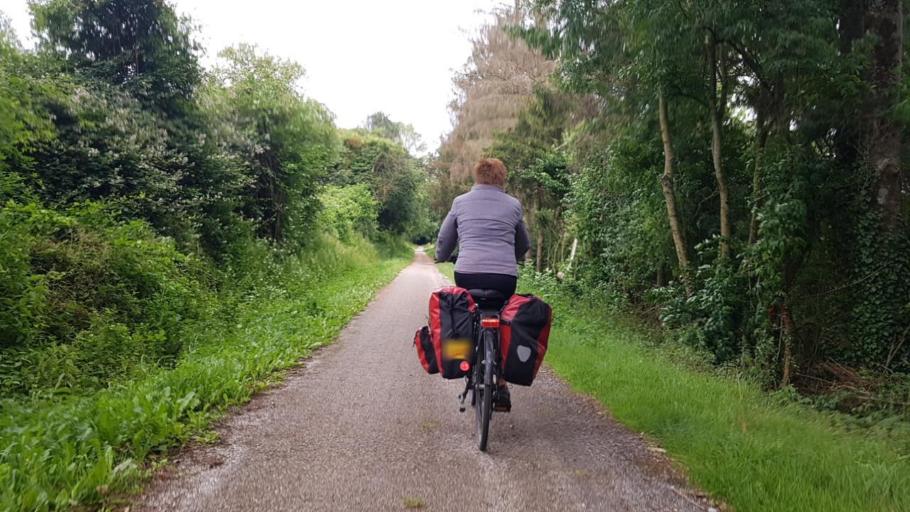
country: FR
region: Picardie
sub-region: Departement de l'Aisne
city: La Capelle
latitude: 49.9059
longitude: 3.9073
